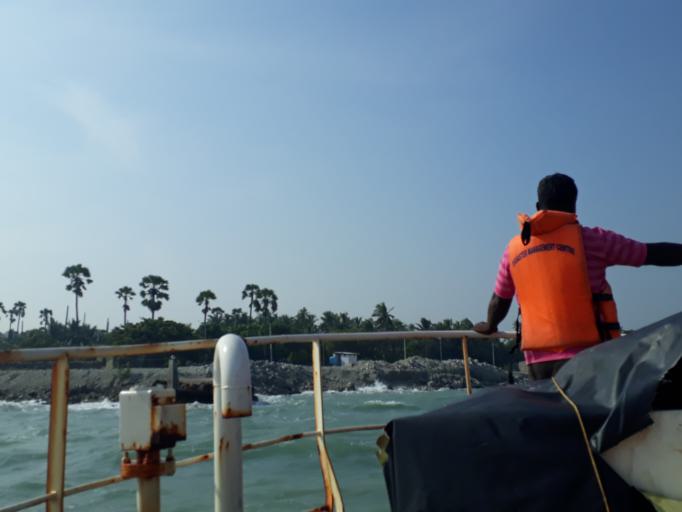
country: LK
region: Northern Province
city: Jaffna
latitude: 9.5298
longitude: 79.7182
